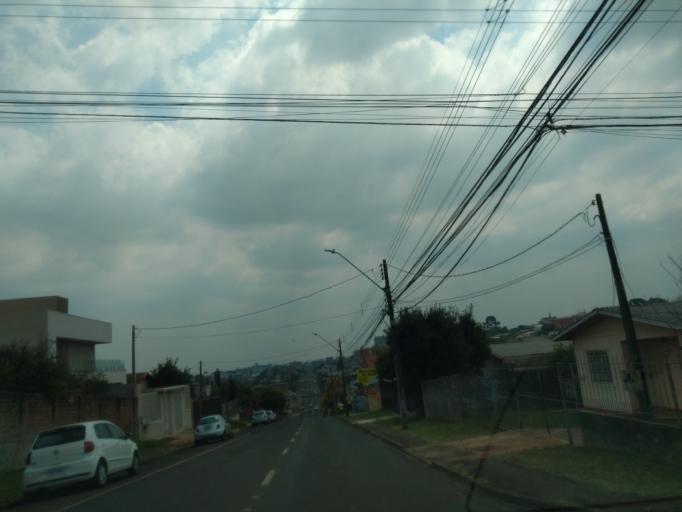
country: BR
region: Parana
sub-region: Guarapuava
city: Guarapuava
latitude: -25.3838
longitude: -51.4795
